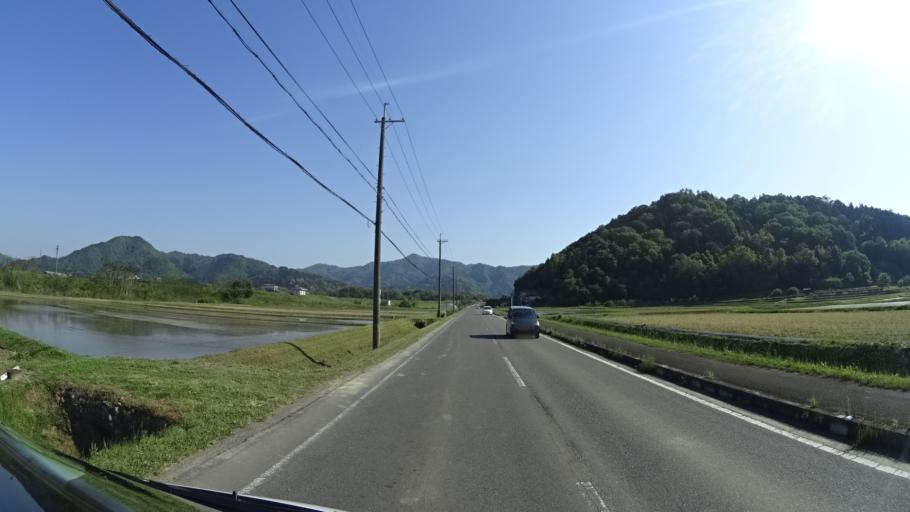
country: JP
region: Kyoto
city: Ayabe
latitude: 35.3154
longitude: 135.2092
